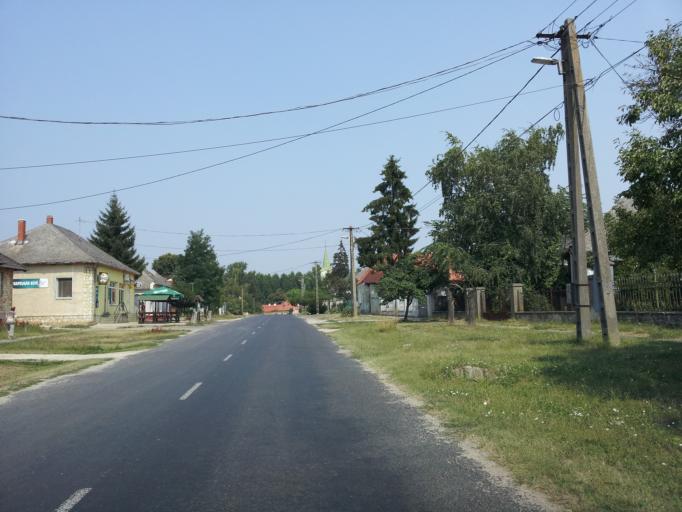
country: HU
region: Gyor-Moson-Sopron
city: Bakonyszentlaszlo
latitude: 47.4482
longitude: 17.7914
